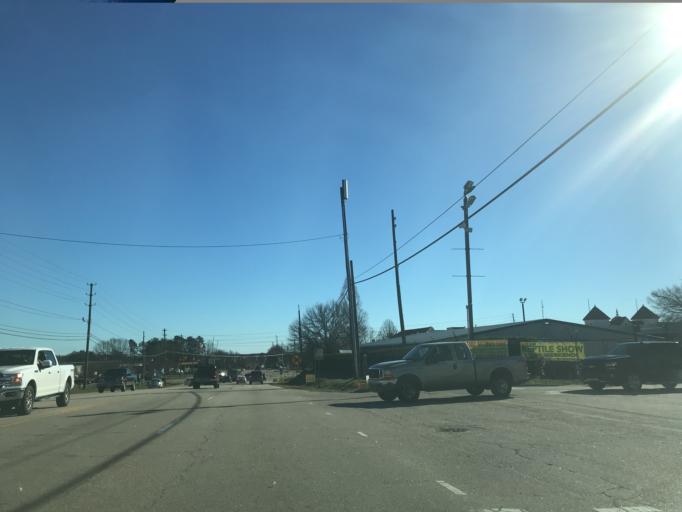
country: US
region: North Carolina
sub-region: Wake County
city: West Raleigh
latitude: 35.7960
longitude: -78.7072
